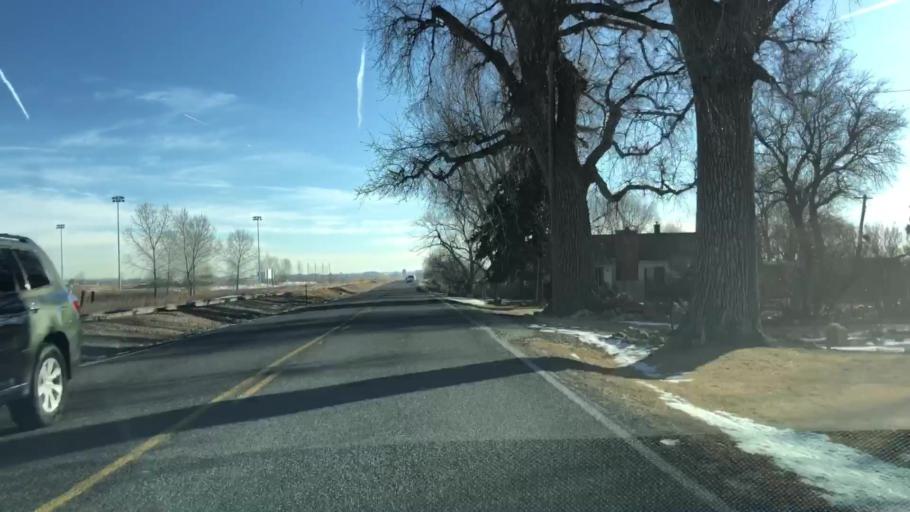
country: US
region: Colorado
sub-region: Larimer County
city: Loveland
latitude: 40.3999
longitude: -105.0181
